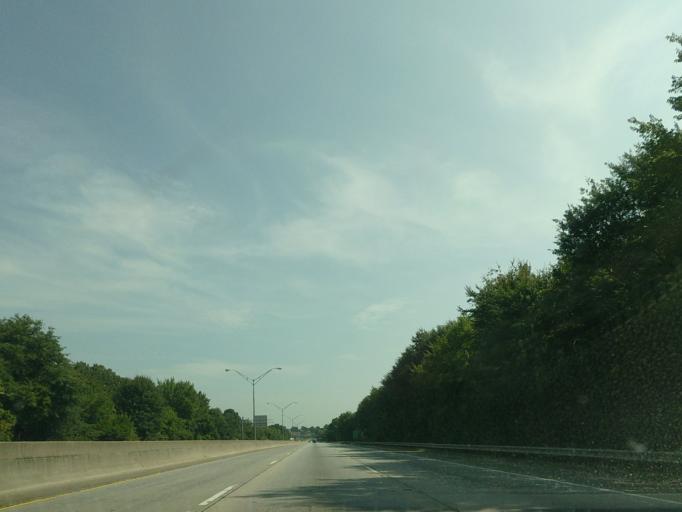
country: US
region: Georgia
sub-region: Bibb County
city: Macon
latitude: 32.8044
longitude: -83.6582
